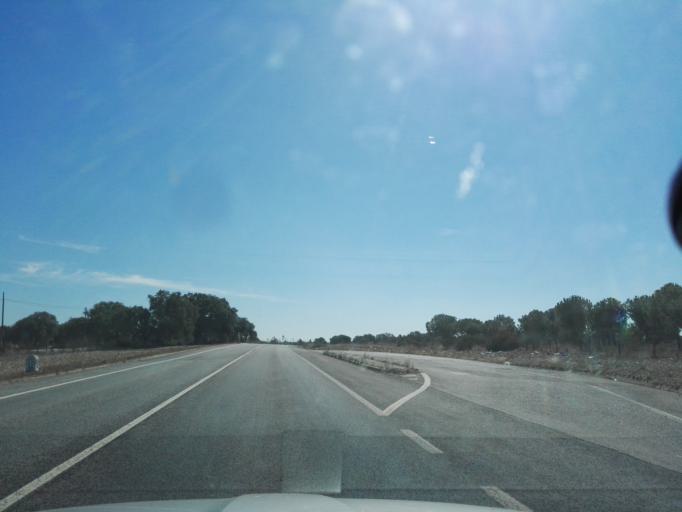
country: PT
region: Santarem
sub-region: Benavente
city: Poceirao
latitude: 38.8577
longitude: -8.7778
